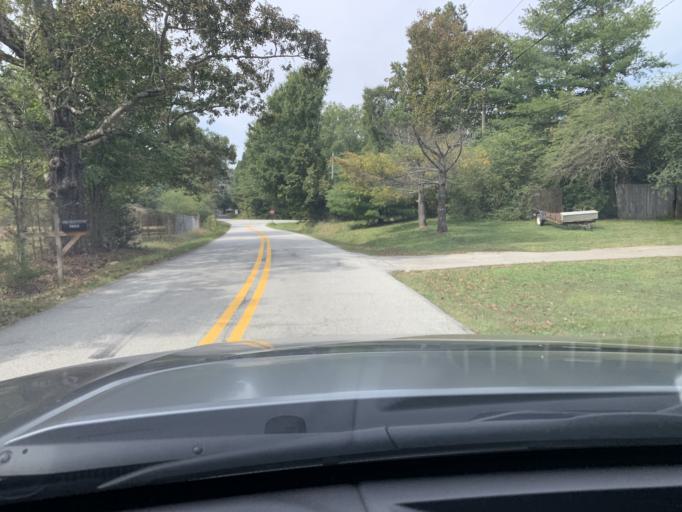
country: US
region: Georgia
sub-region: Polk County
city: Cedartown
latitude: 33.9751
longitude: -85.2930
